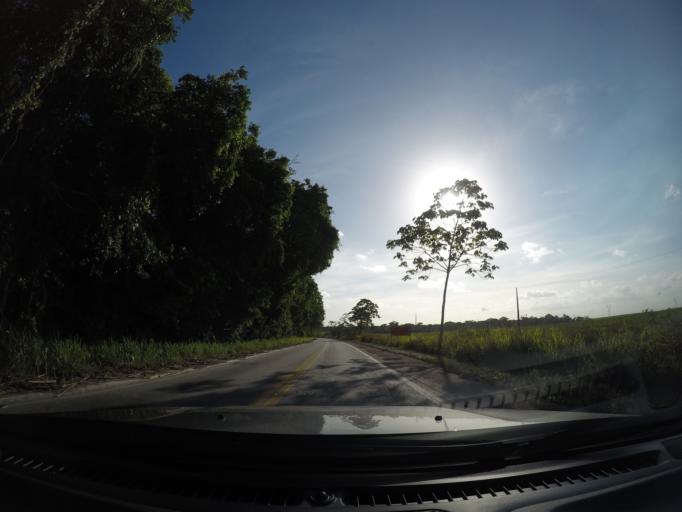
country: BR
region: Alagoas
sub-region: Rio Largo
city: Rio Largo
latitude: -9.5123
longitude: -35.9315
